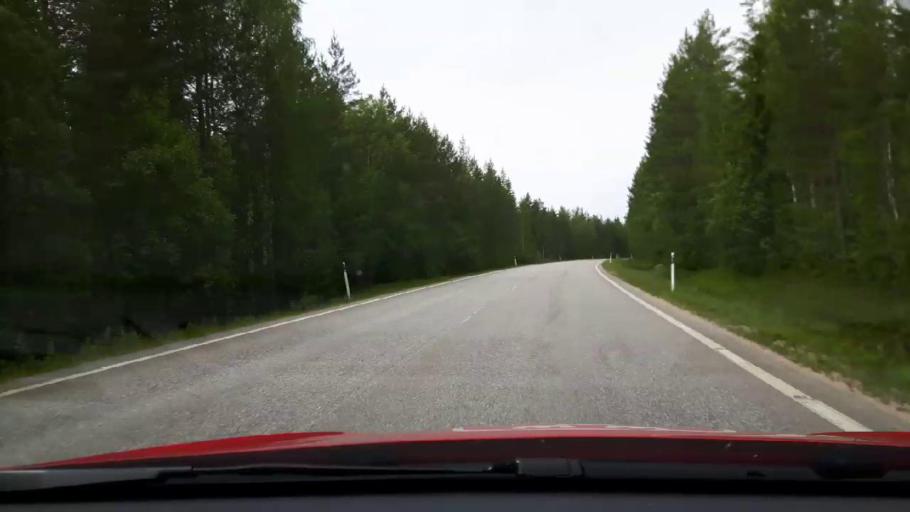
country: SE
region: Jaemtland
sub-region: Harjedalens Kommun
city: Sveg
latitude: 62.1017
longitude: 14.2114
